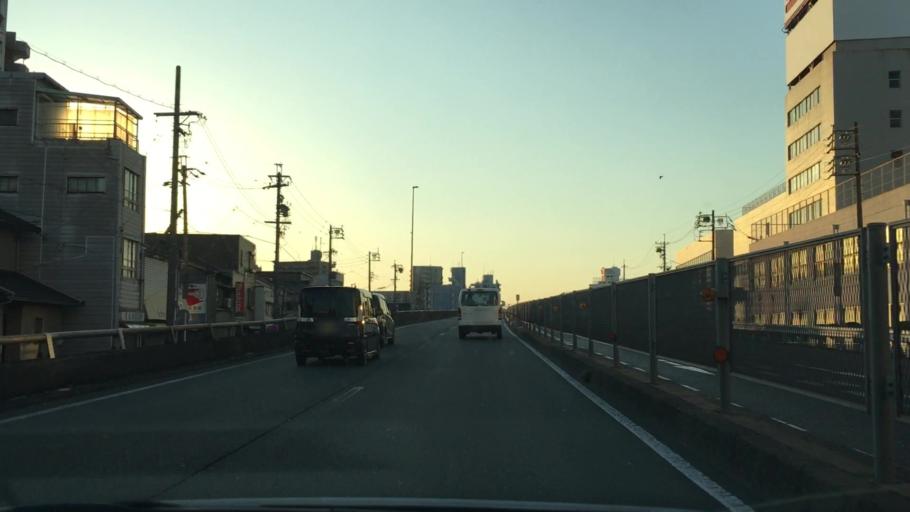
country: JP
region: Aichi
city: Nagoya-shi
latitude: 35.1166
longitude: 136.9178
